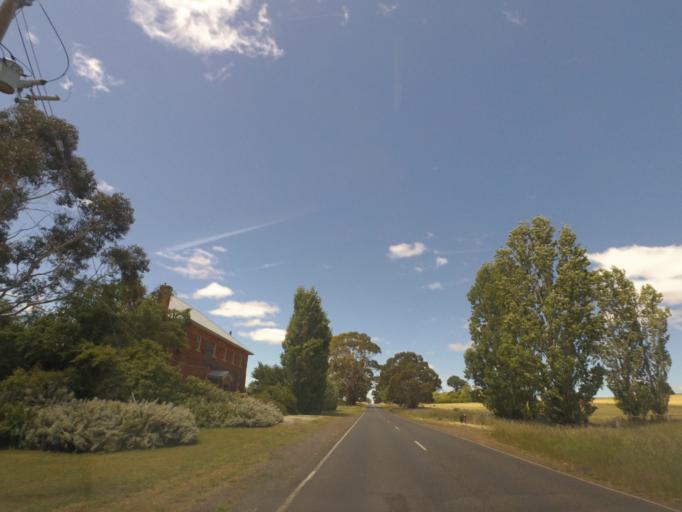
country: AU
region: Victoria
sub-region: Mount Alexander
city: Castlemaine
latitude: -37.3226
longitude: 144.1976
